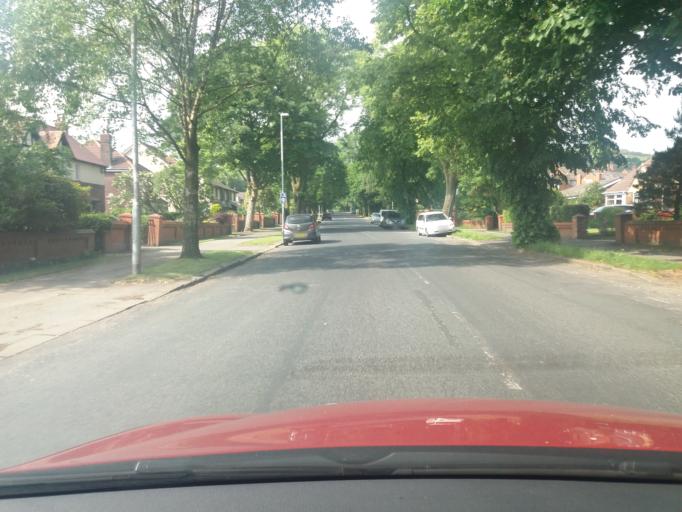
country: GB
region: England
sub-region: Borough of Bolton
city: Horwich
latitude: 53.6051
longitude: -2.5518
